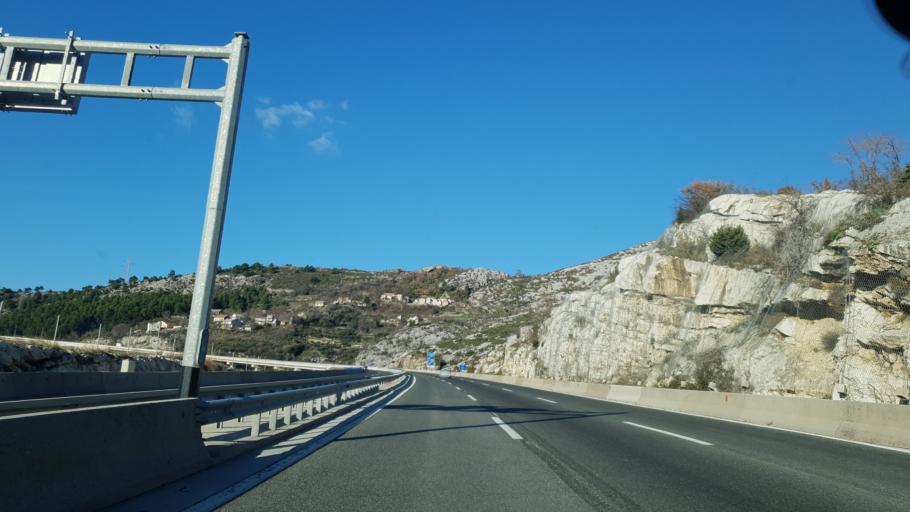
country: HR
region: Splitsko-Dalmatinska
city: Klis
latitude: 43.5557
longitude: 16.5387
